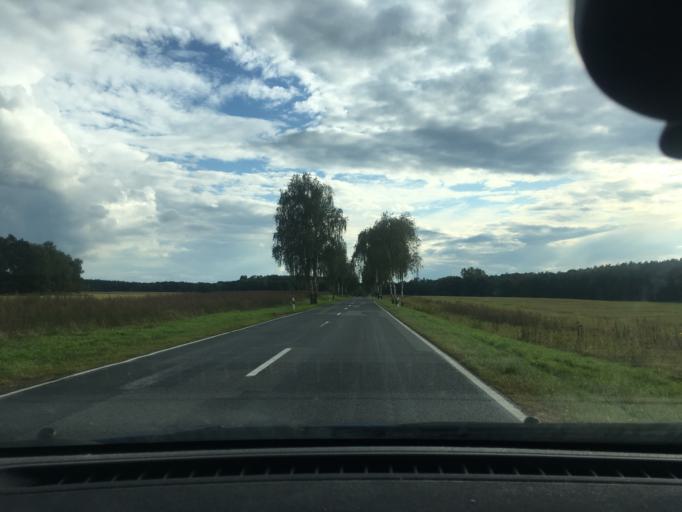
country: DE
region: Lower Saxony
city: Neu Darchau
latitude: 53.2200
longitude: 10.8809
